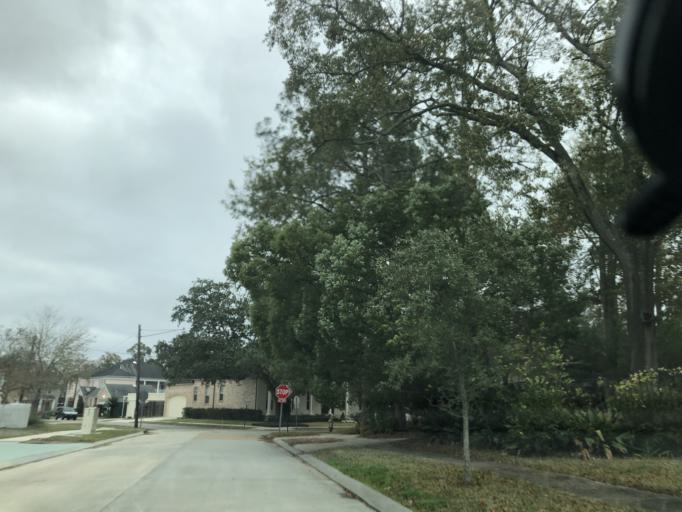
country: US
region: Louisiana
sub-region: Jefferson Parish
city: Metairie
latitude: 29.9825
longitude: -90.1495
